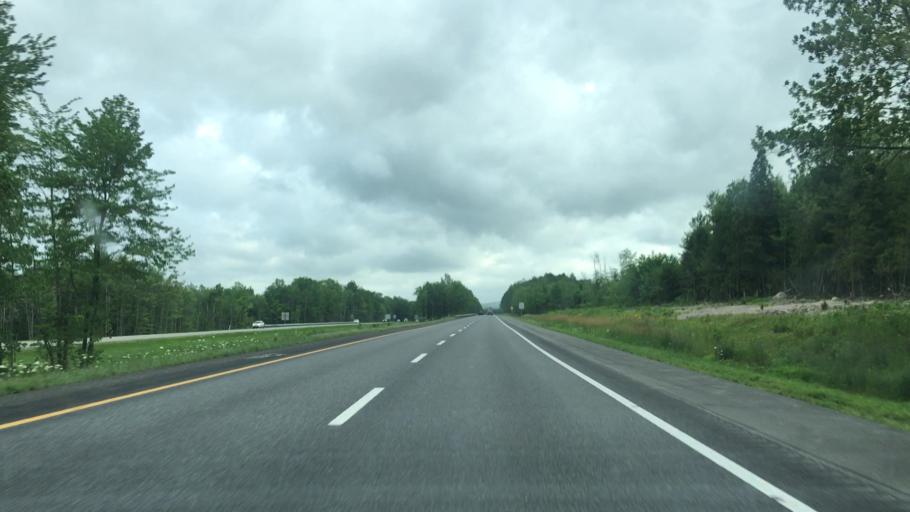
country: US
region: Maine
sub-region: Kennebec County
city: Oakland
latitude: 44.5399
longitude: -69.6837
